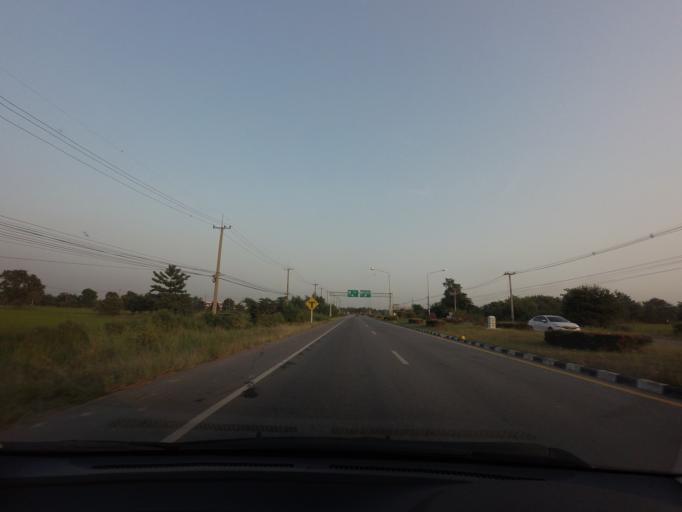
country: TH
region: Sukhothai
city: Kong Krailat
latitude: 17.0086
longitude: 99.9265
